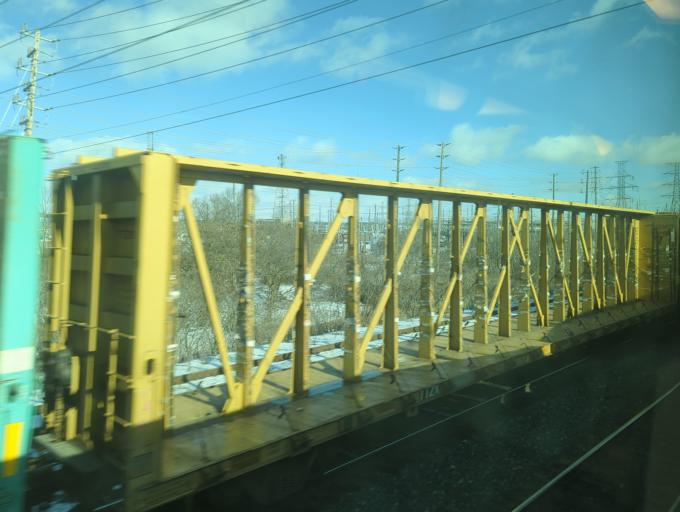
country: CA
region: Ontario
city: Burlington
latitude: 43.3265
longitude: -79.8331
